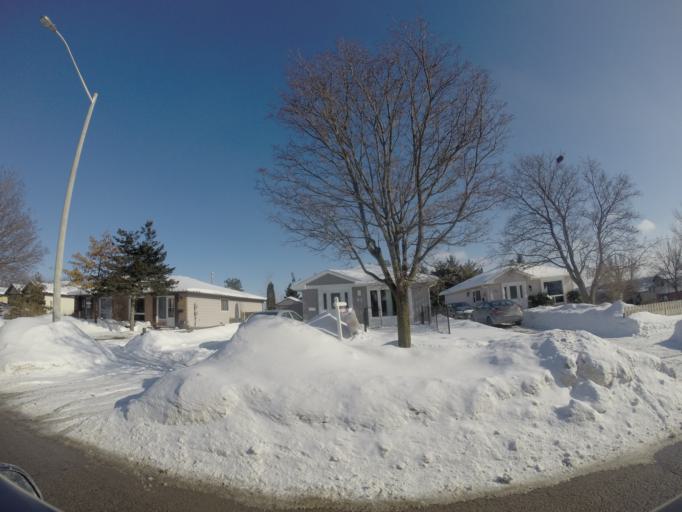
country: CA
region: Ontario
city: Barrie
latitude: 44.3867
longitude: -79.7206
